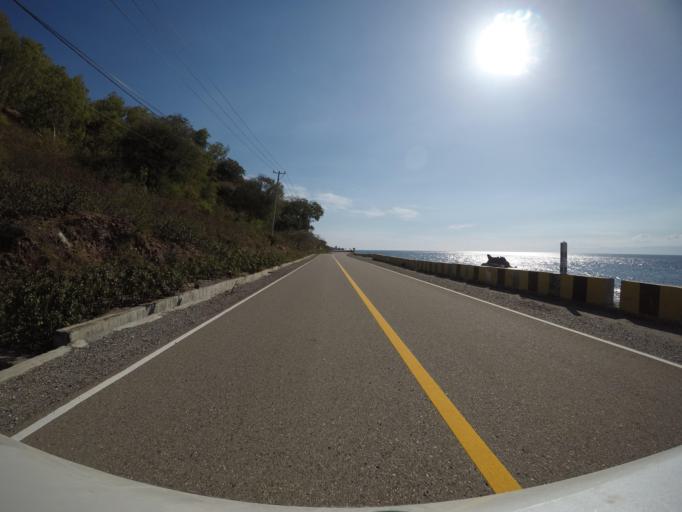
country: TL
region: Liquica
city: Maubara
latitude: -8.6120
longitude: 125.1945
